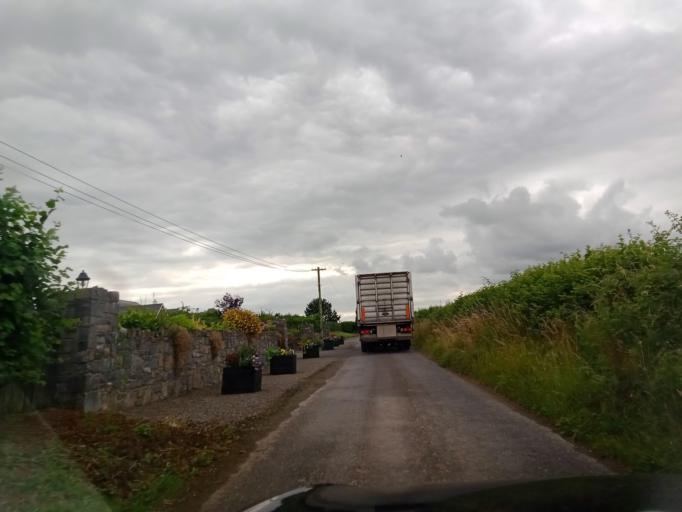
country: IE
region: Leinster
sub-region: Laois
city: Stradbally
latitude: 52.9614
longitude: -7.1698
